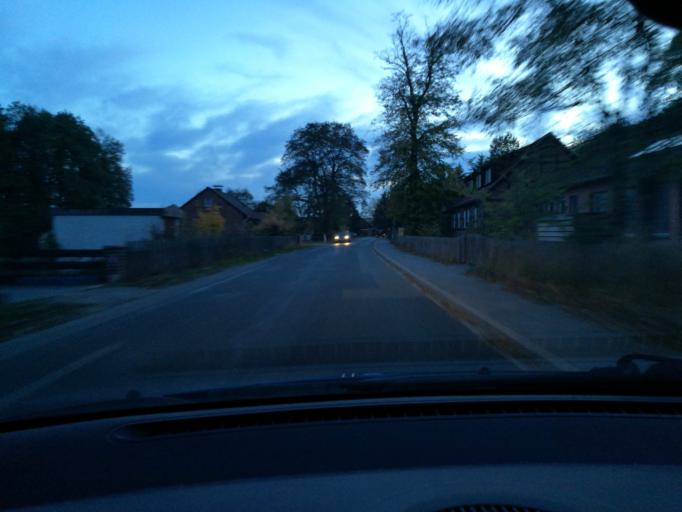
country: DE
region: Lower Saxony
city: Gartow
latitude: 53.0579
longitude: 11.4551
